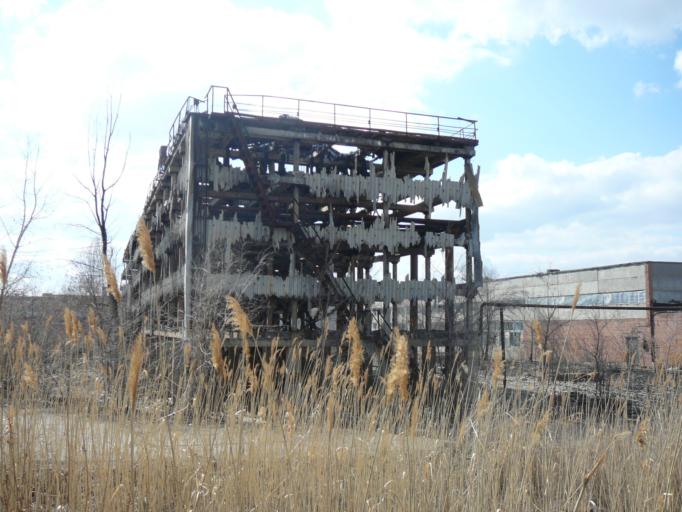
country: RU
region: Saratov
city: Engel's
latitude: 51.4679
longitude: 46.1642
